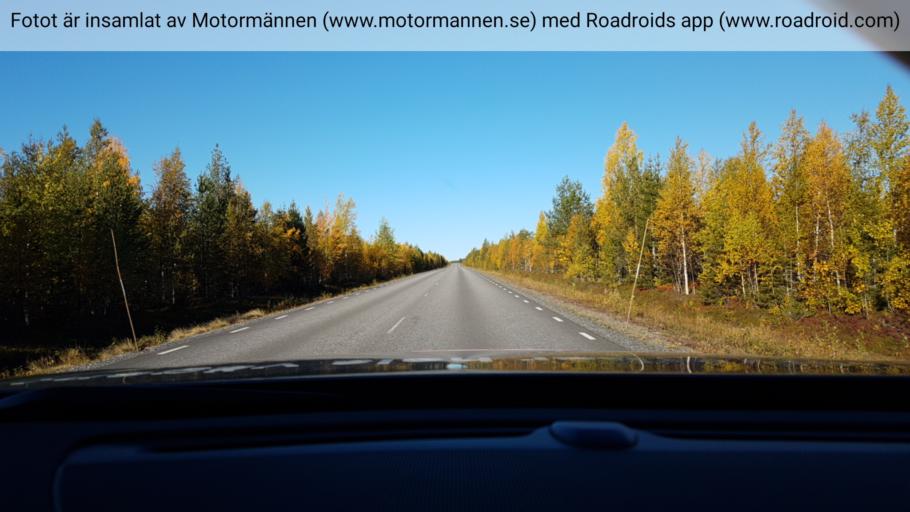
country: SE
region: Vaesterbotten
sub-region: Skelleftea Kommun
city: Storvik
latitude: 65.3253
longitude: 20.6939
